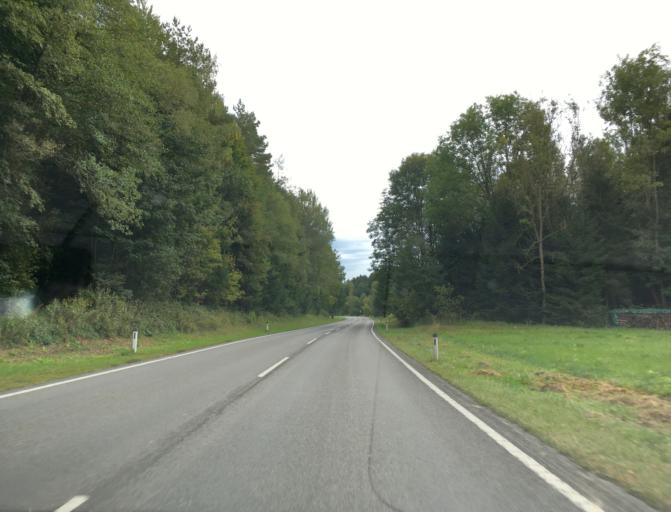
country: AT
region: Lower Austria
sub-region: Politischer Bezirk Neunkirchen
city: Thomasberg
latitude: 47.5353
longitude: 16.1703
